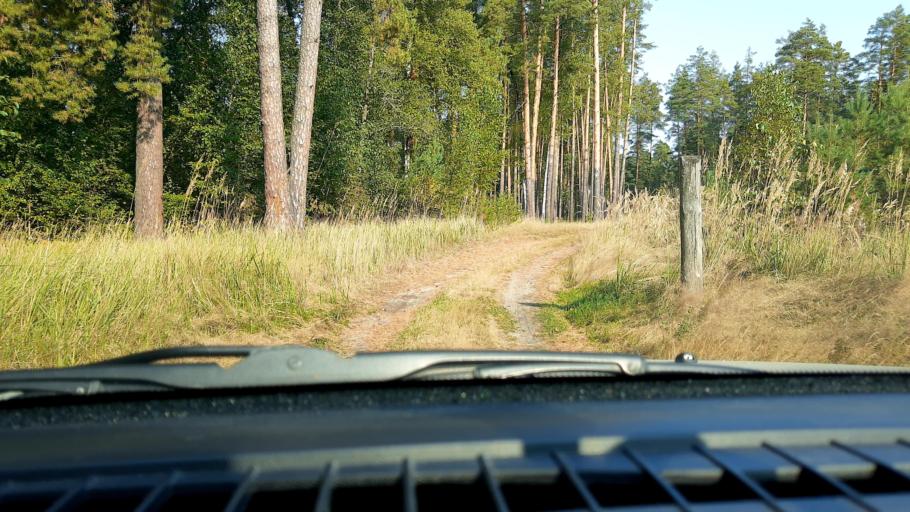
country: RU
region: Nizjnij Novgorod
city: Lukino
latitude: 56.4054
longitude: 43.6329
